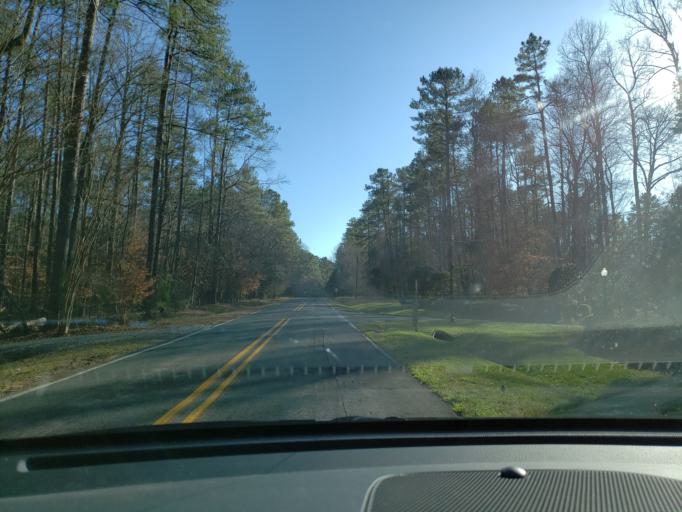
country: US
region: North Carolina
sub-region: Orange County
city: Chapel Hill
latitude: 35.9840
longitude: -79.0487
